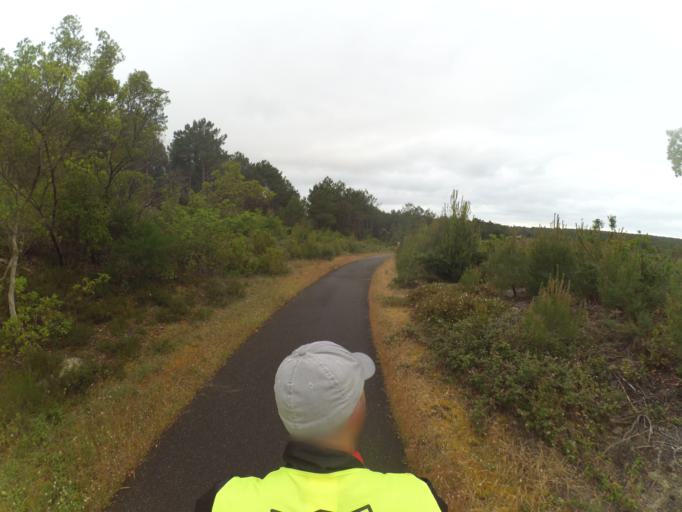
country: FR
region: Aquitaine
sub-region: Departement des Landes
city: Mimizan
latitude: 44.2193
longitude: -1.2758
